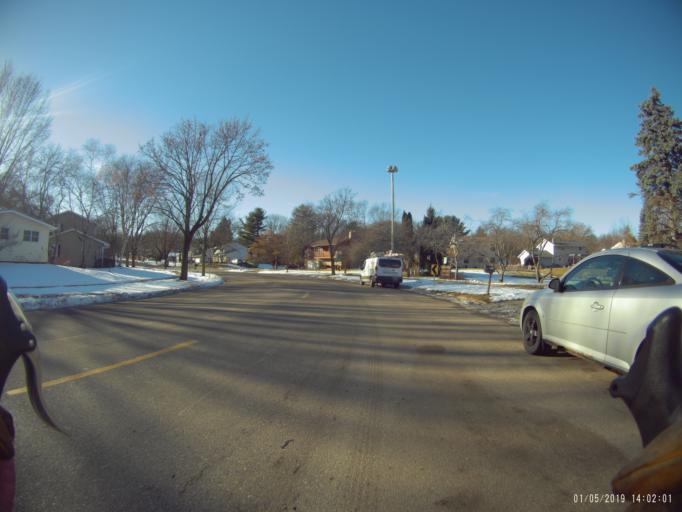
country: US
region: Wisconsin
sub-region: Dane County
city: Madison
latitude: 43.0270
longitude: -89.4253
